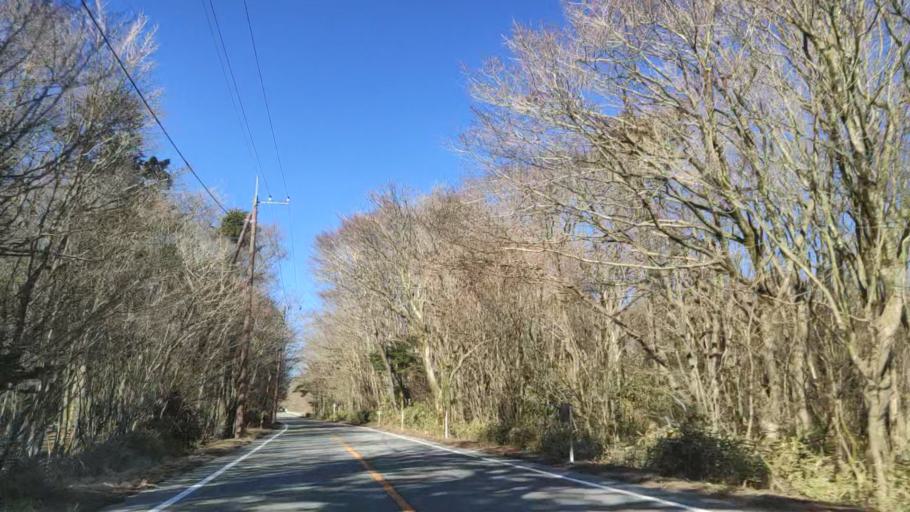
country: JP
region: Yamanashi
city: Fujikawaguchiko
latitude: 35.4296
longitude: 138.6335
